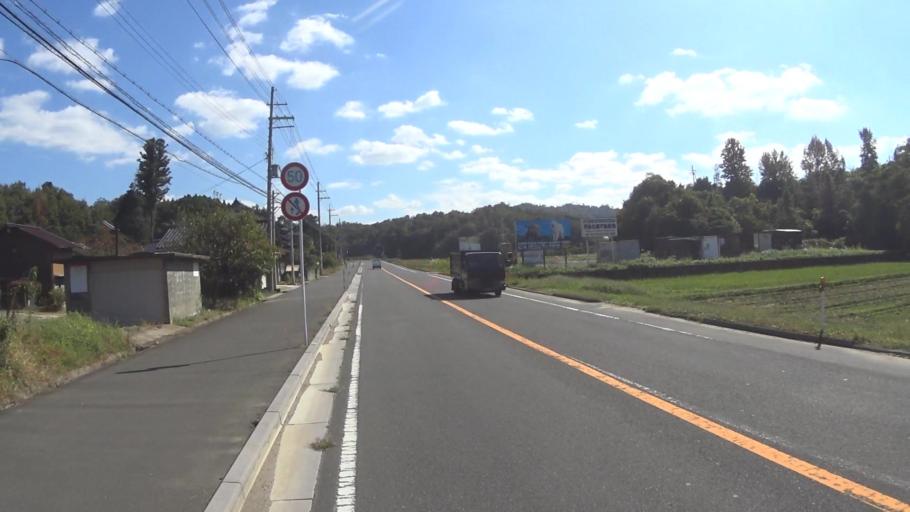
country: JP
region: Hyogo
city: Toyooka
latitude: 35.5889
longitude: 134.9433
